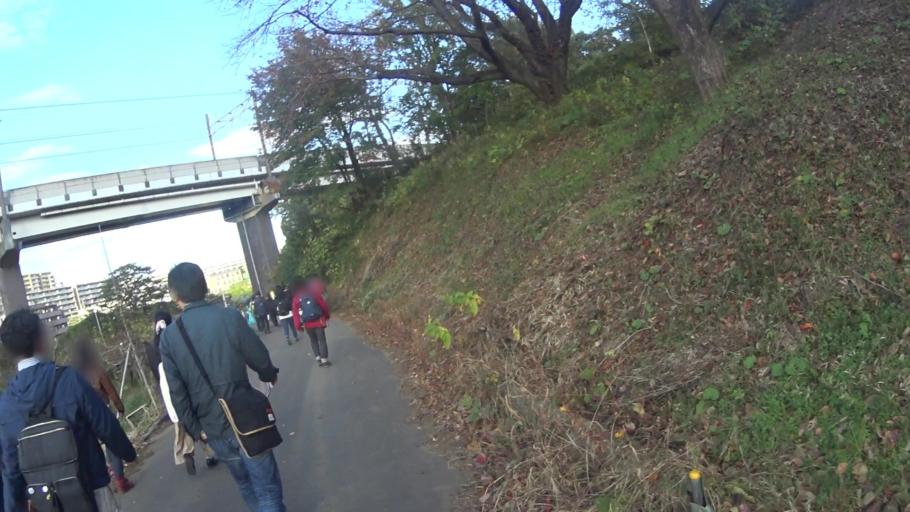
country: JP
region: Tokyo
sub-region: Machida-shi
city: Machida
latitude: 35.6184
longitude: 139.4754
